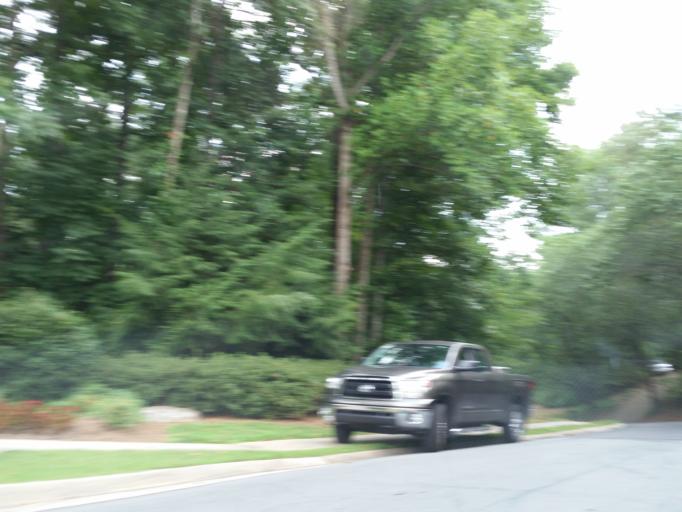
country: US
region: Georgia
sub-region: Fulton County
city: Roswell
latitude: 34.0491
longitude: -84.4330
